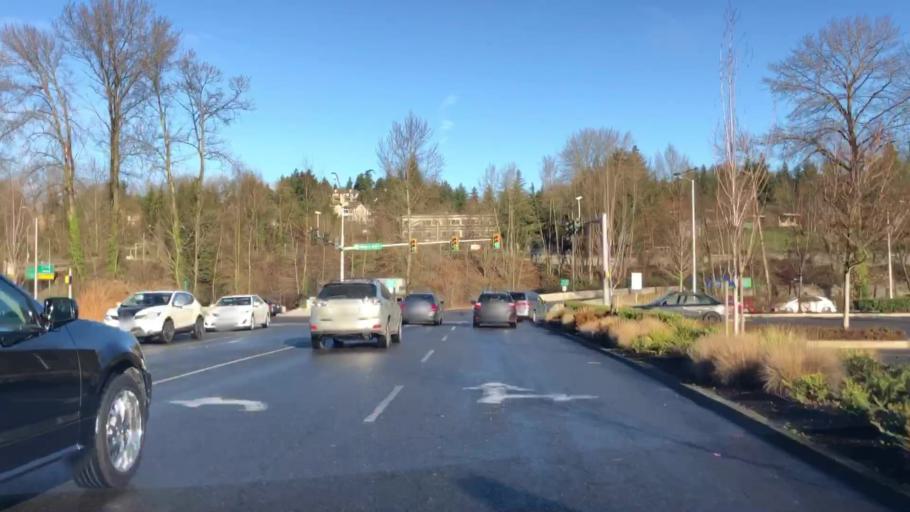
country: US
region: Washington
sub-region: King County
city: Tukwila
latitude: 47.4607
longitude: -122.2564
